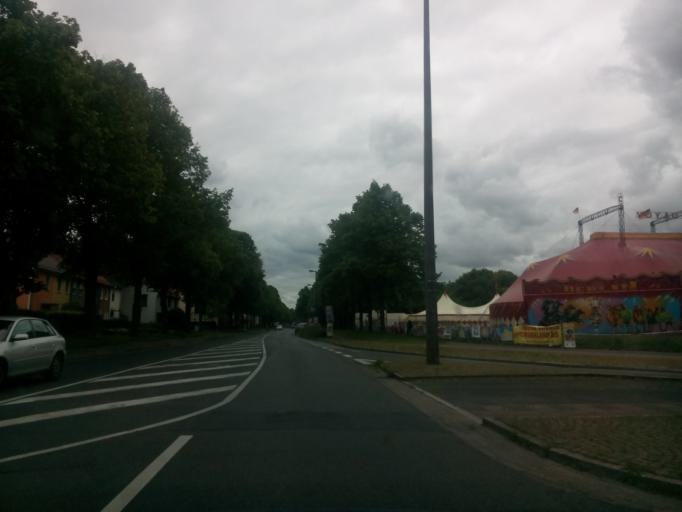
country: DE
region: Lower Saxony
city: Neuenkirchen
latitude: 53.1922
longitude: 8.5624
